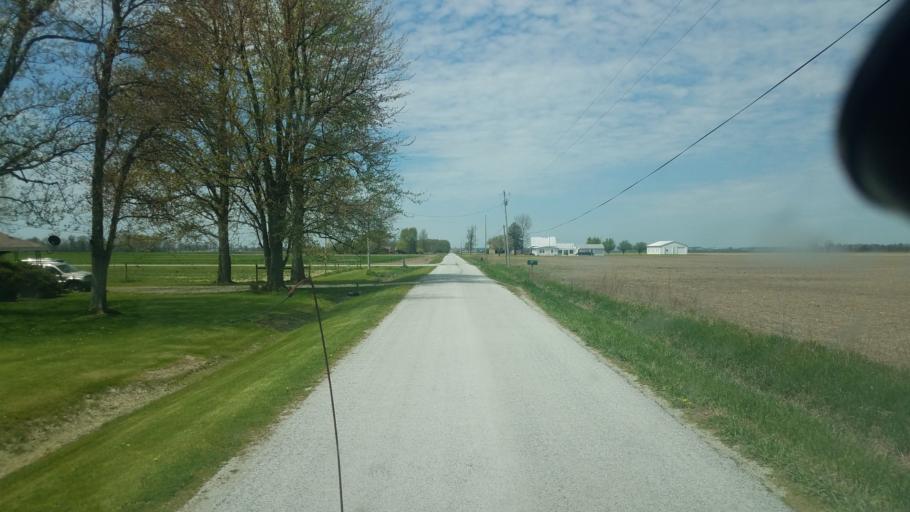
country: US
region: Ohio
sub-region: Hardin County
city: Ada
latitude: 40.6574
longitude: -83.7488
